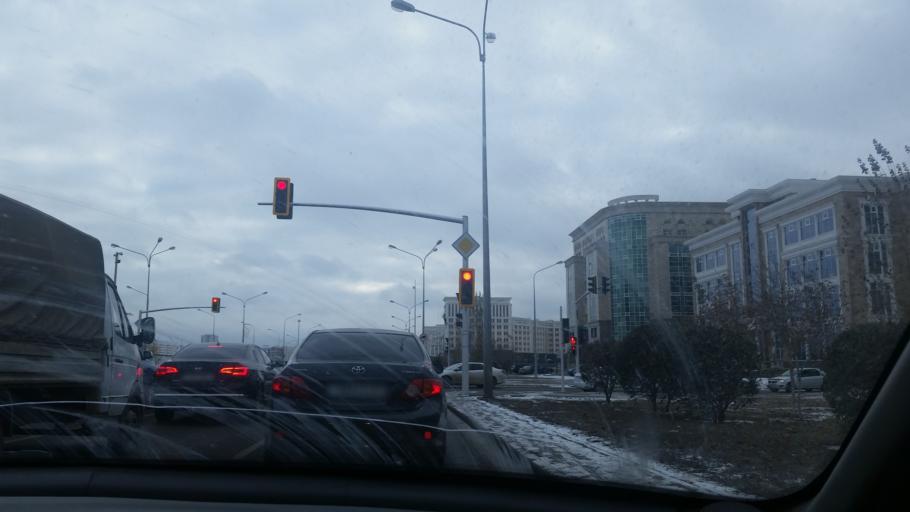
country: KZ
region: Astana Qalasy
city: Astana
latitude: 51.1091
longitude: 71.4316
